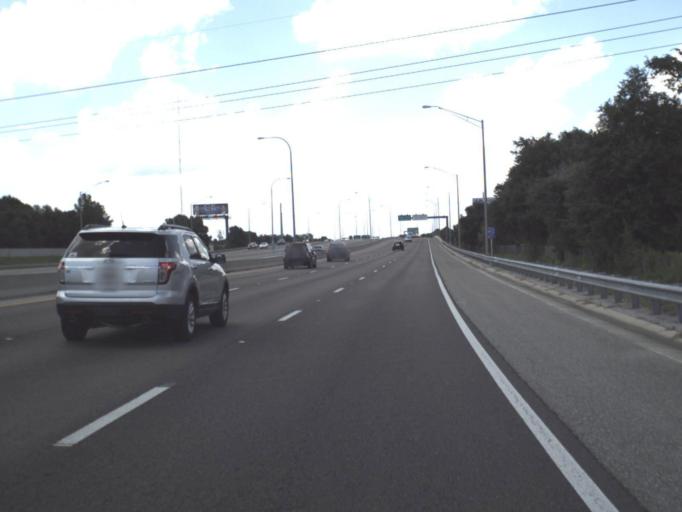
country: US
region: Florida
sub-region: Hillsborough County
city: Palm River-Clair Mel
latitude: 27.9365
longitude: -82.3584
